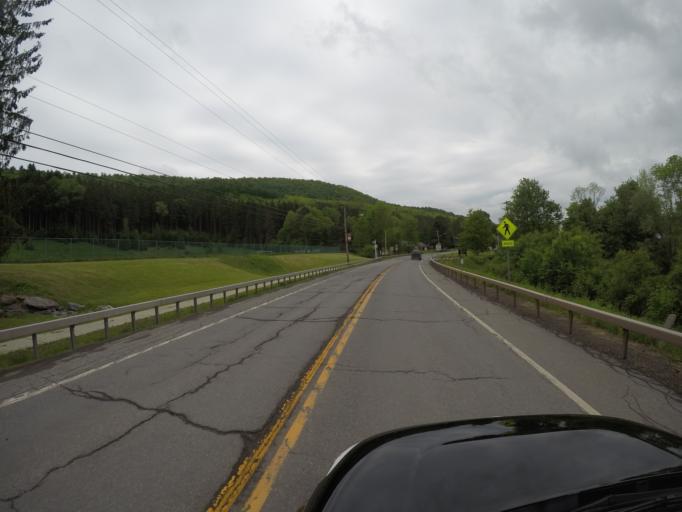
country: US
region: New York
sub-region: Delaware County
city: Delhi
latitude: 42.2693
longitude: -74.9155
